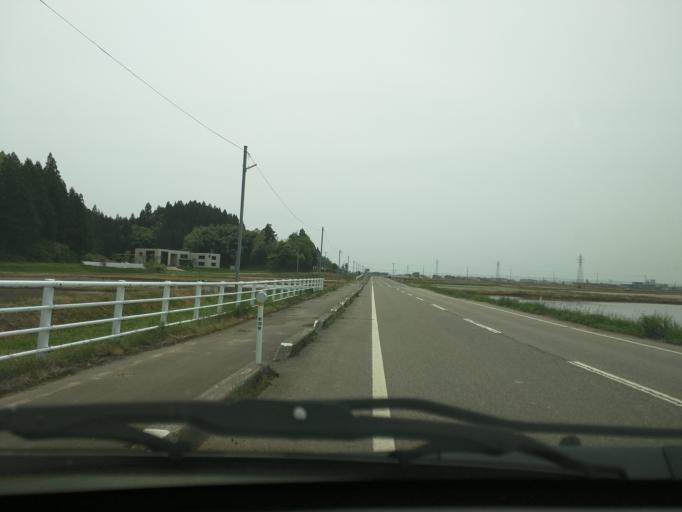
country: JP
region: Niigata
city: Sanjo
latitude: 37.5767
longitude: 138.9507
